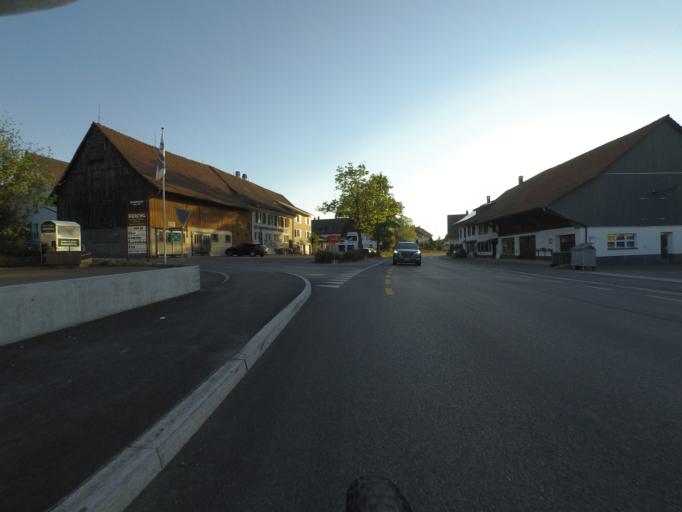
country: CH
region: Thurgau
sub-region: Frauenfeld District
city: Gachnang
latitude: 47.5397
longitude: 8.8222
